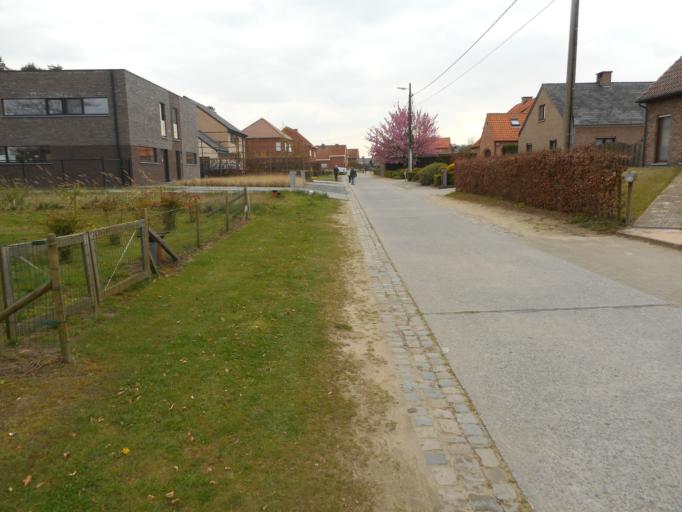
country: BE
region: Flanders
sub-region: Provincie Vlaams-Brabant
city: Begijnendijk
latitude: 50.9941
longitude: 4.8037
